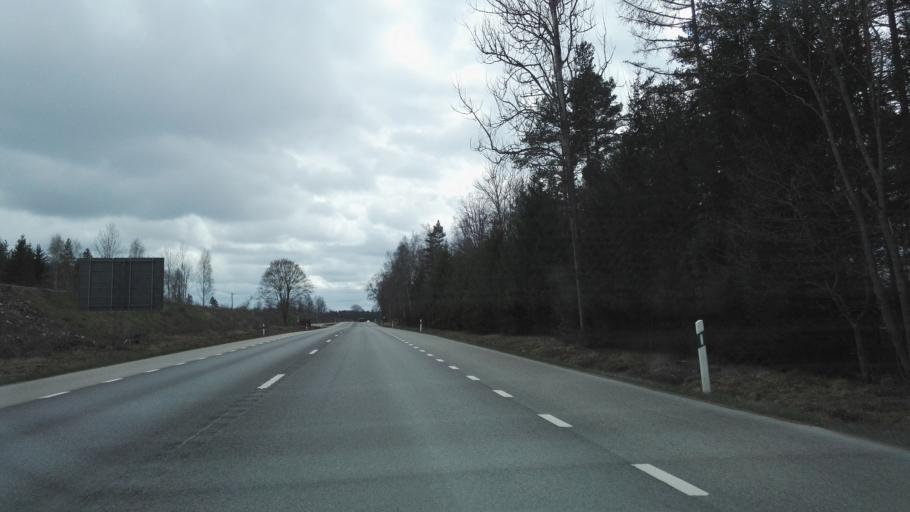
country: SE
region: Kronoberg
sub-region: Vaxjo Kommun
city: Vaexjoe
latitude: 56.8752
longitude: 14.7422
